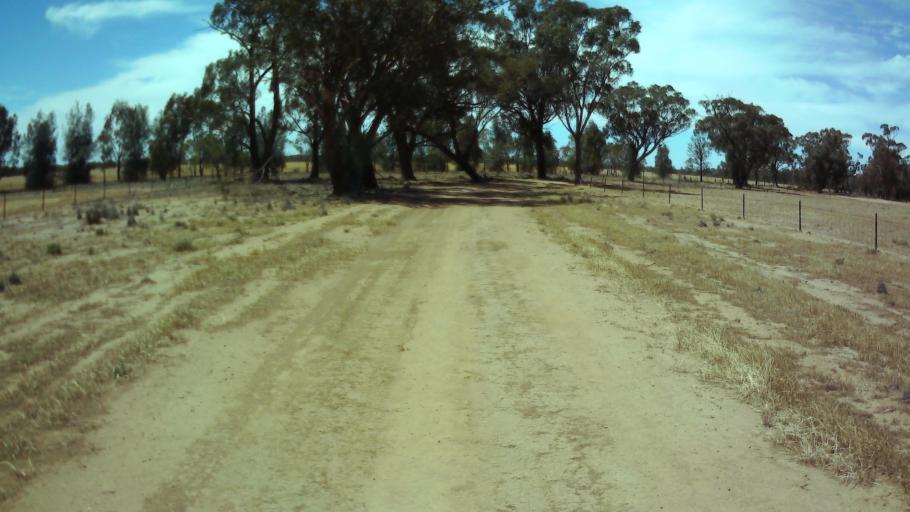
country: AU
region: New South Wales
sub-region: Weddin
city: Grenfell
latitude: -33.9035
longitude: 147.8073
